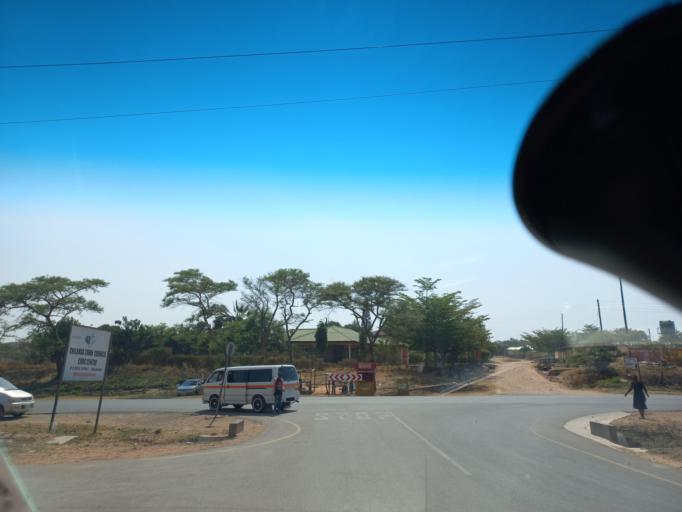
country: ZM
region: Lusaka
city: Lusaka
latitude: -15.5698
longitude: 28.2715
